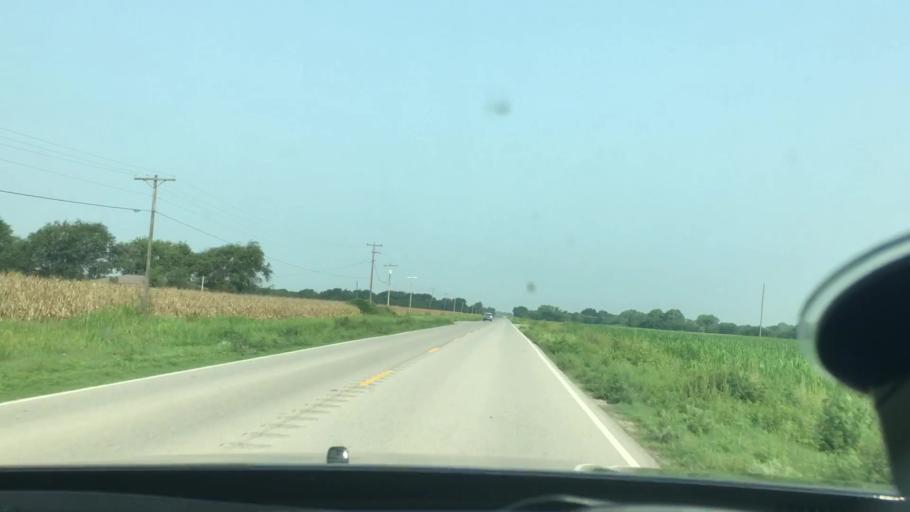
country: US
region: Oklahoma
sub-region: Garvin County
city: Maysville
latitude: 34.7797
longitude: -97.3252
